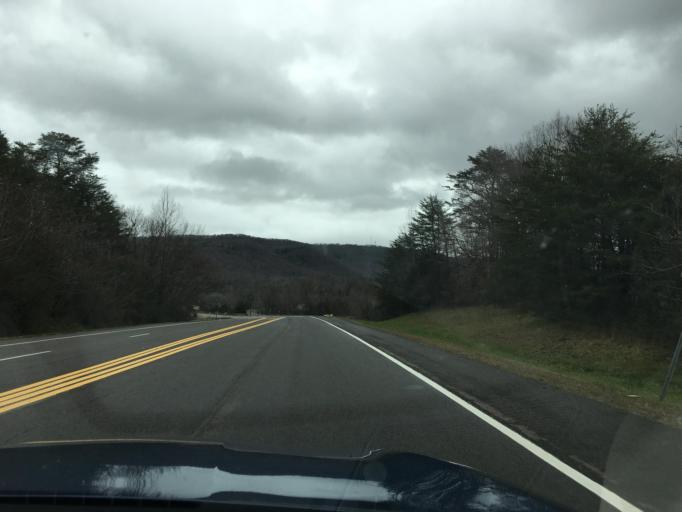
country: US
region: Tennessee
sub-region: Rhea County
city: Spring City
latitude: 35.6945
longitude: -84.8702
